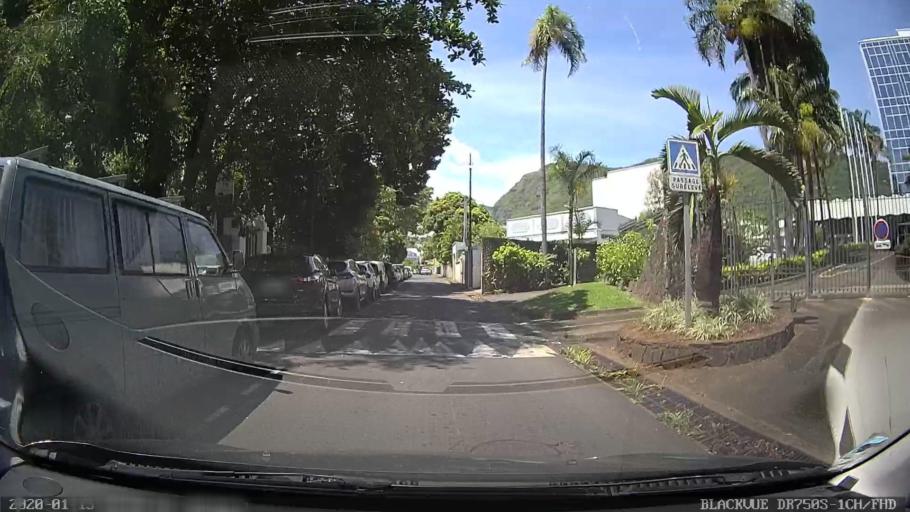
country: RE
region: Reunion
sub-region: Reunion
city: Saint-Denis
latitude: -20.8869
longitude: 55.4499
